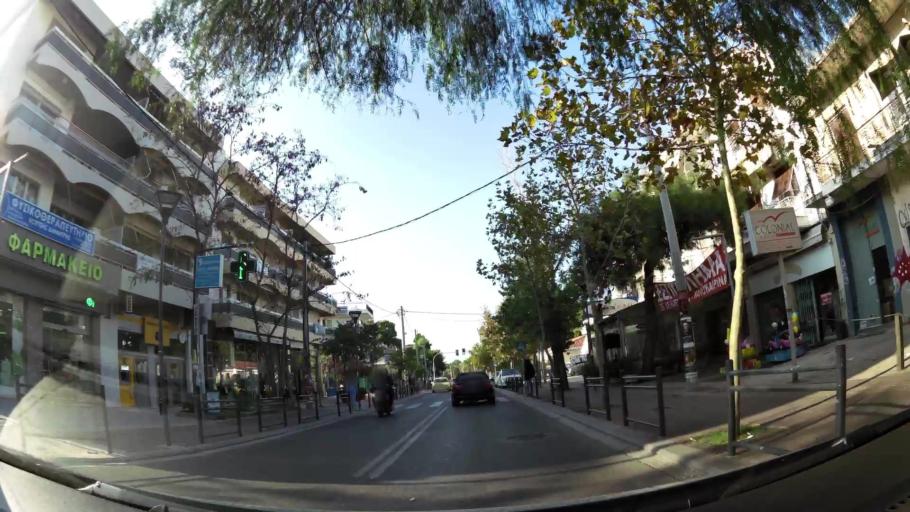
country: GR
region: Attica
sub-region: Nomarchia Athinas
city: Agia Paraskevi
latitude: 38.0097
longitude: 23.8249
